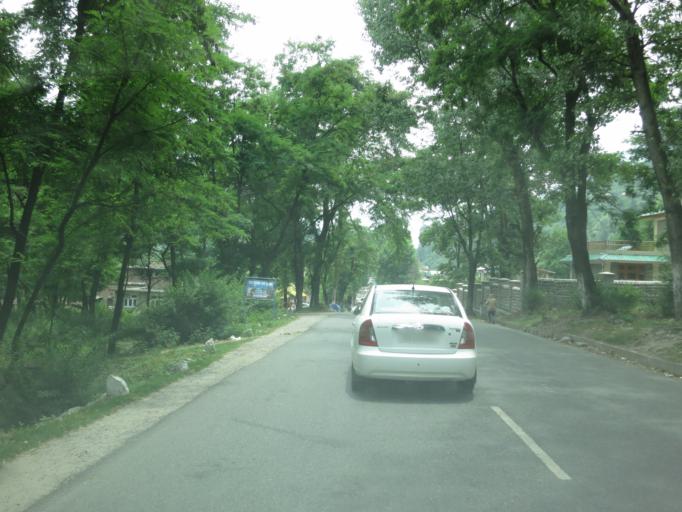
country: IN
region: Himachal Pradesh
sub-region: Kulu
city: Nagar
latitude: 32.1634
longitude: 77.1760
